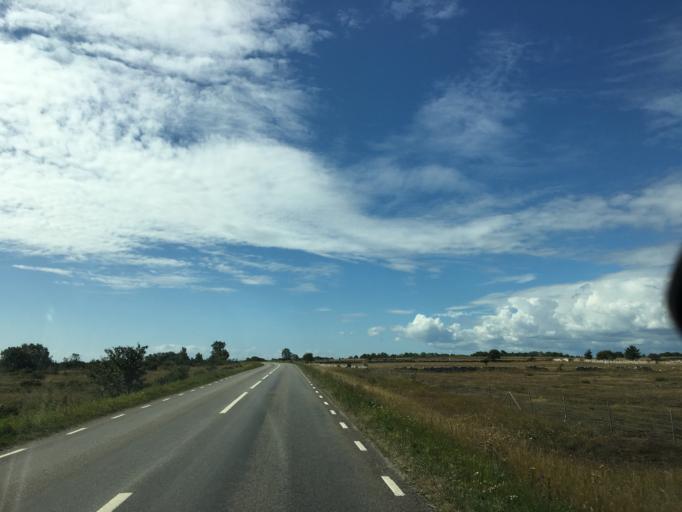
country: SE
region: Kalmar
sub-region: Morbylanga Kommun
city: Moerbylanga
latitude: 56.5002
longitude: 16.4281
